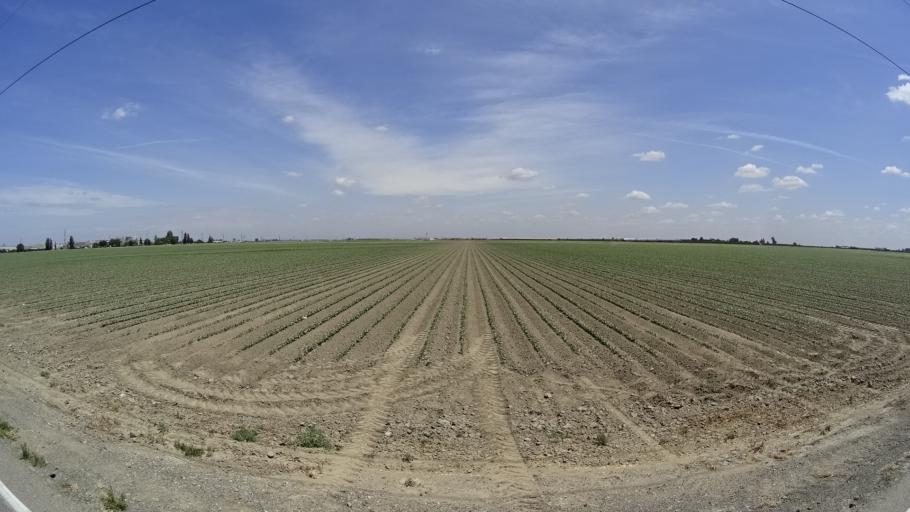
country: US
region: California
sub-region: Kings County
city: Home Garden
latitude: 36.2502
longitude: -119.6548
